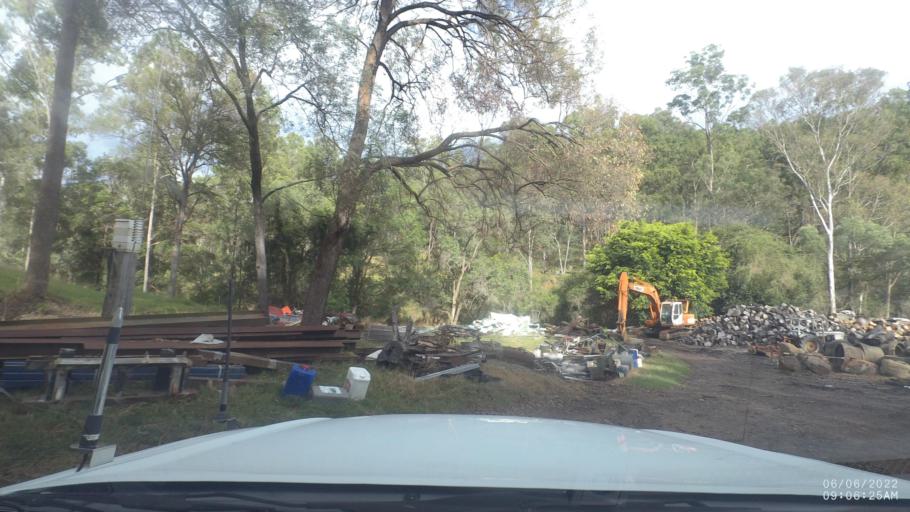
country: AU
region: Queensland
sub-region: Ipswich
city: Deebing Heights
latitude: -27.7692
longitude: 152.8116
